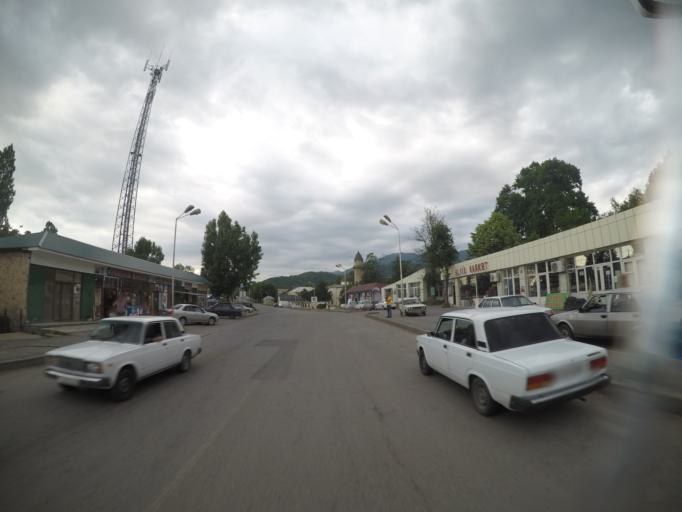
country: AZ
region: Qabala Rayon
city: Qutqashen
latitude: 40.9462
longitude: 47.9424
